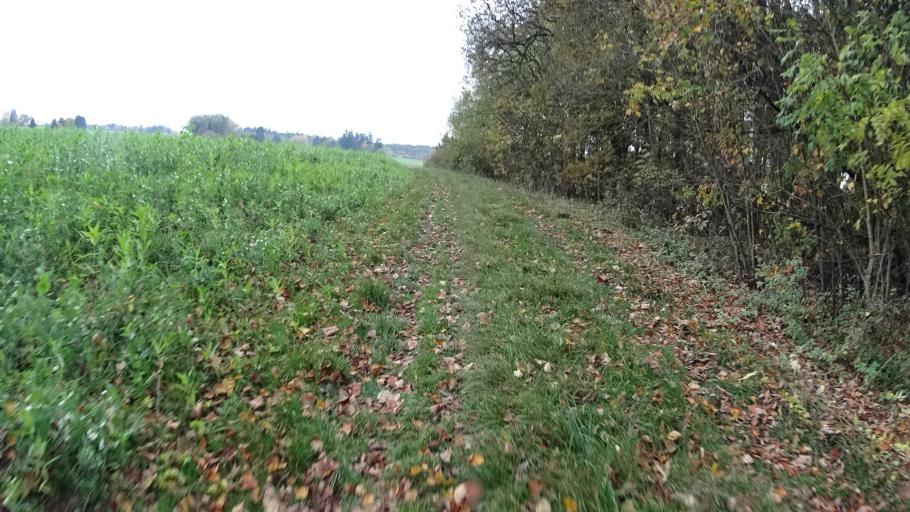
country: DE
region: Bavaria
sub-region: Upper Bavaria
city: Hitzhofen
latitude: 48.8580
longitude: 11.2998
